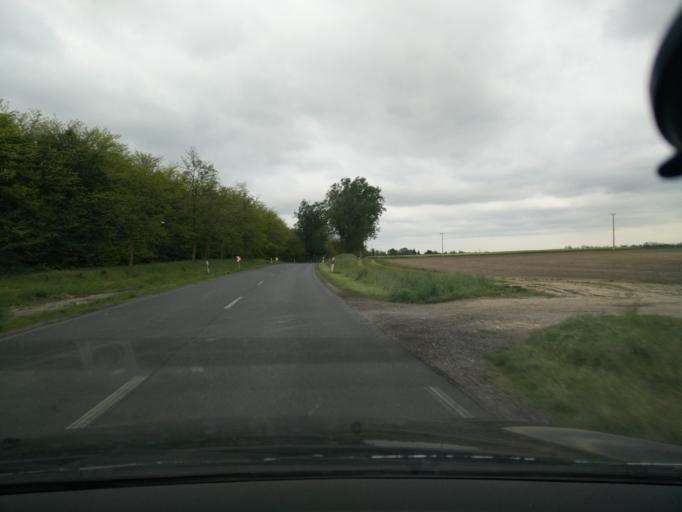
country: HU
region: Veszprem
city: Papa
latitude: 47.3844
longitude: 17.4683
